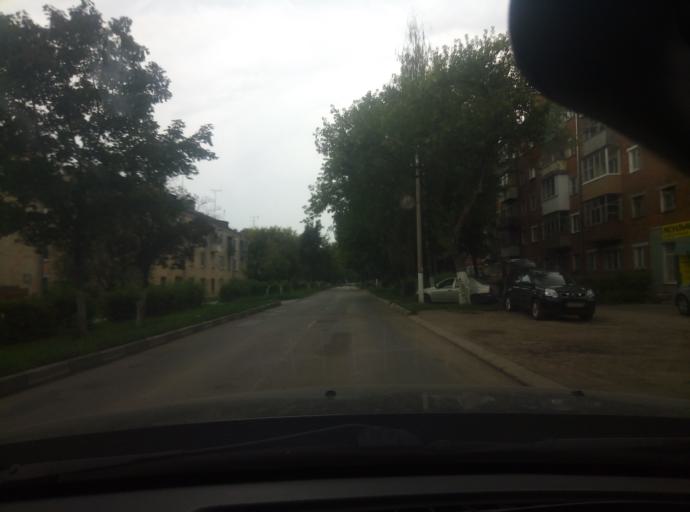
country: RU
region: Tula
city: Tula
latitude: 54.2111
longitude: 37.6734
